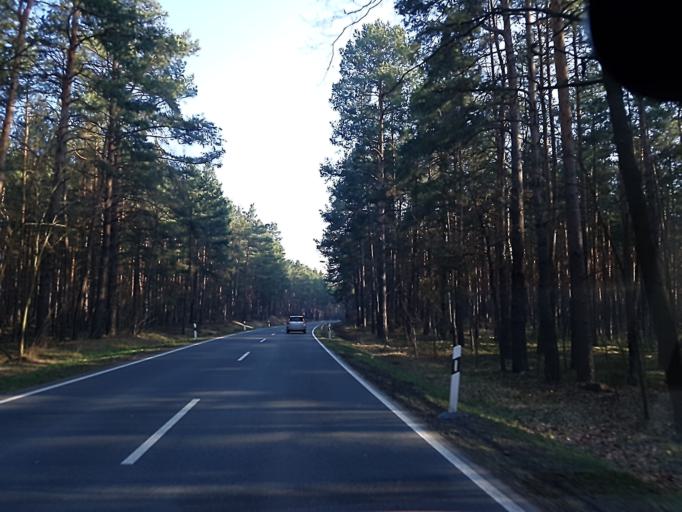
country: DE
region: Brandenburg
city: Calau
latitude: 51.7136
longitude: 13.9210
